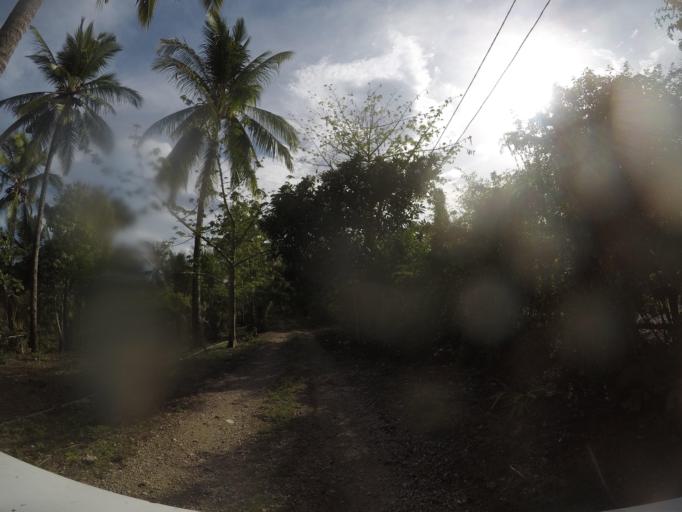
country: TL
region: Baucau
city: Baucau
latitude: -8.5066
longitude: 126.4474
